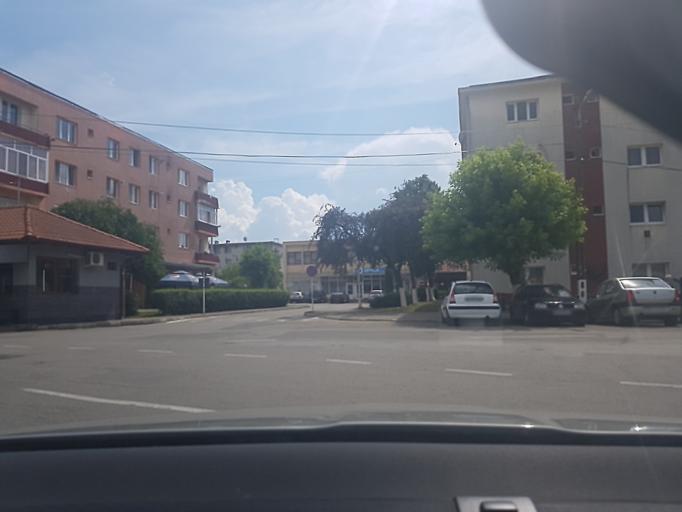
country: RO
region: Hunedoara
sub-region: Comuna Calan
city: Calan
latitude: 45.7326
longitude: 23.0233
